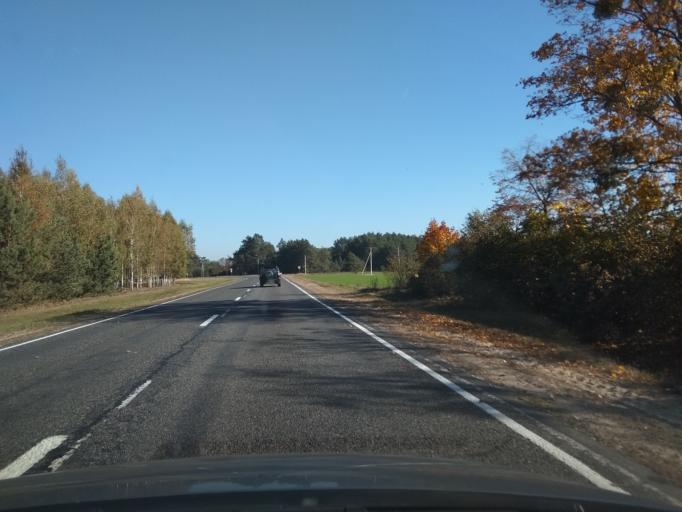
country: BY
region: Brest
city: Kobryn
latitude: 52.1161
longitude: 24.3021
